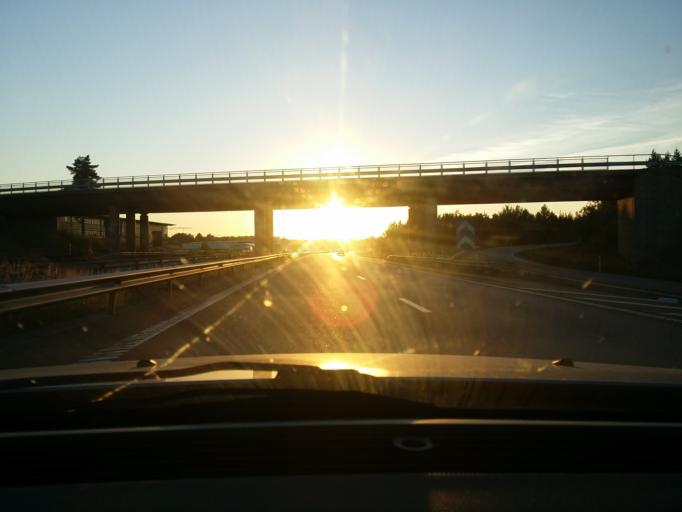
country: SE
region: Uppsala
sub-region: Enkopings Kommun
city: Enkoping
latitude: 59.6475
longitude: 17.1462
